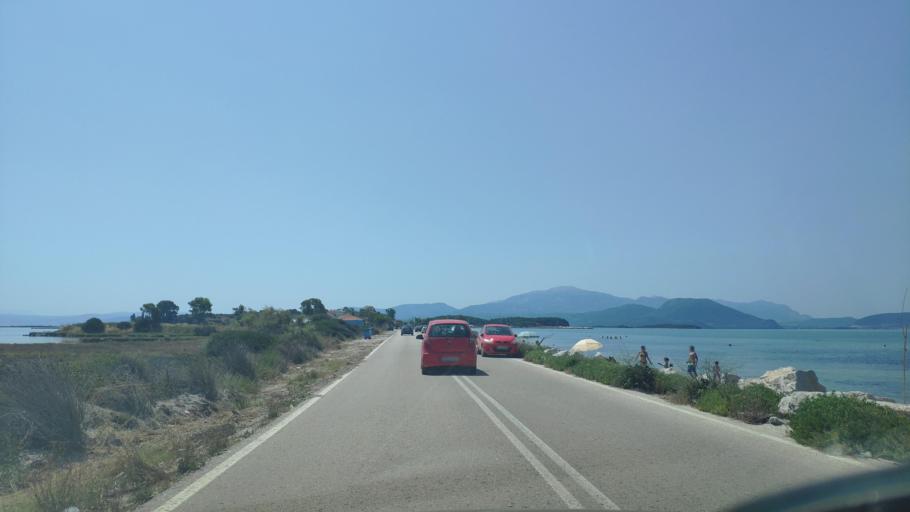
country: GR
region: Epirus
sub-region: Nomos Artas
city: Aneza
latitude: 39.0222
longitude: 20.9101
